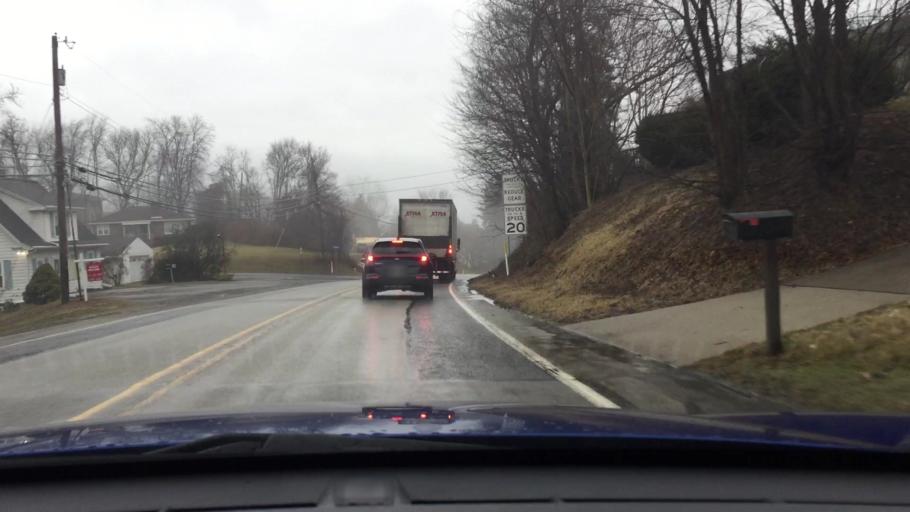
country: US
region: Pennsylvania
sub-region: Washington County
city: Canonsburg
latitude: 40.2449
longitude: -80.1835
